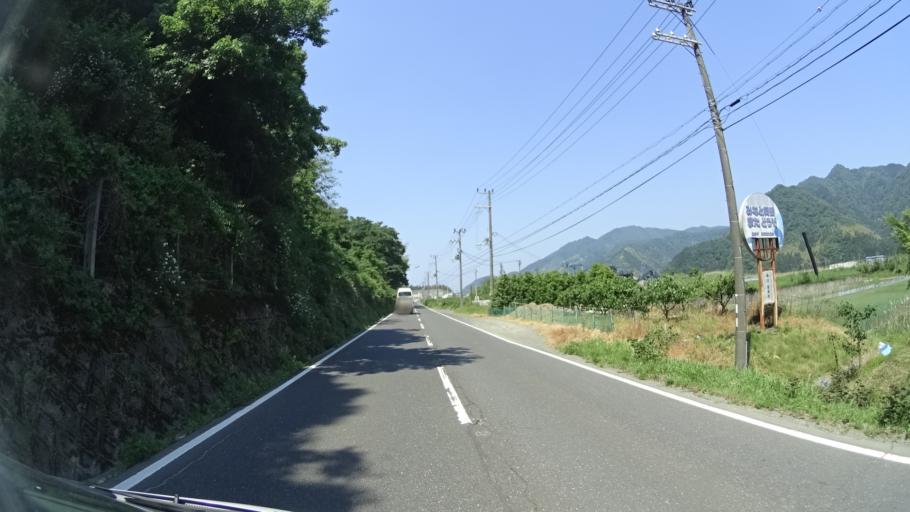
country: JP
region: Kyoto
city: Maizuru
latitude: 35.4852
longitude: 135.2789
